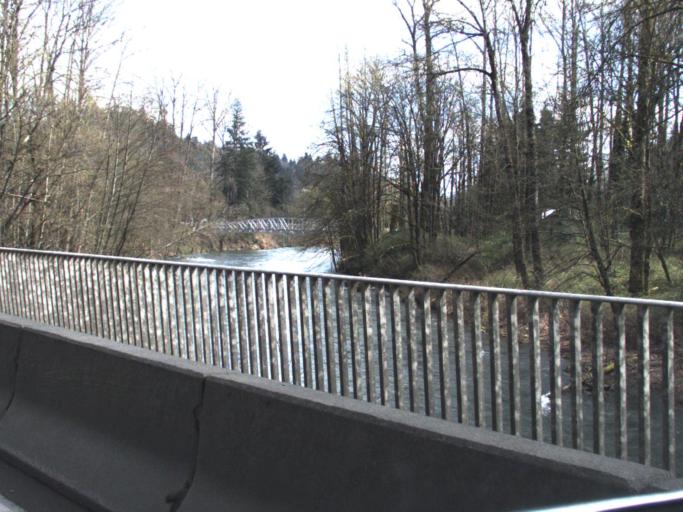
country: US
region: Washington
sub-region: King County
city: Renton
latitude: 47.4772
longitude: -122.1825
